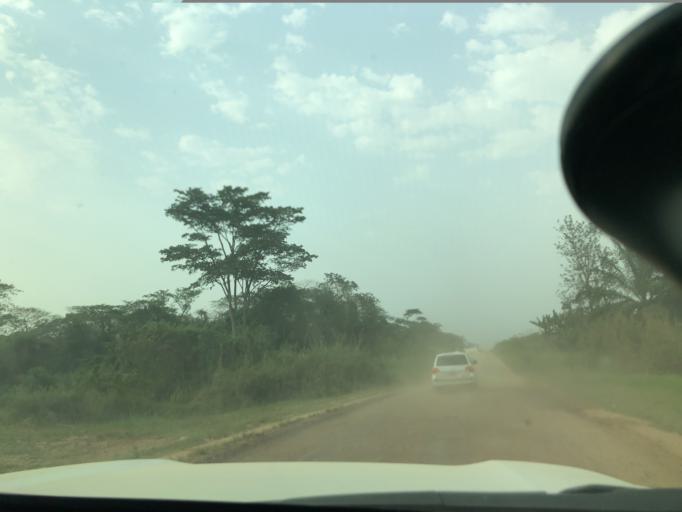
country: UG
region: Western Region
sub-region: Kasese District
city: Margherita
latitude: 0.2230
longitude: 29.6791
